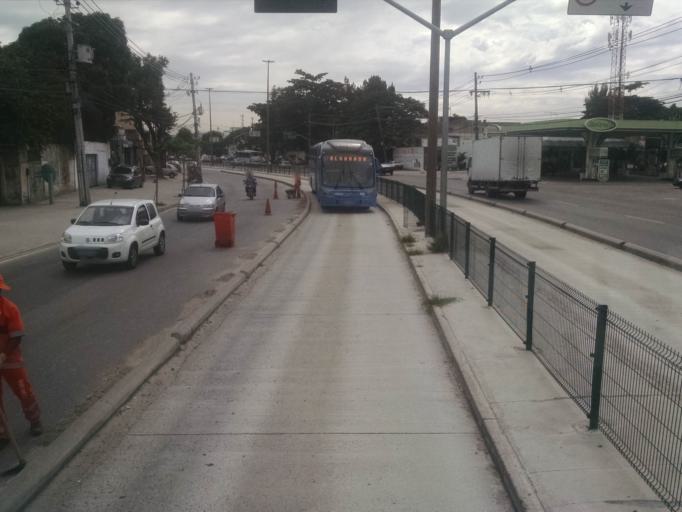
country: BR
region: Rio de Janeiro
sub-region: Sao Joao De Meriti
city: Sao Joao de Meriti
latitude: -22.9473
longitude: -43.3721
